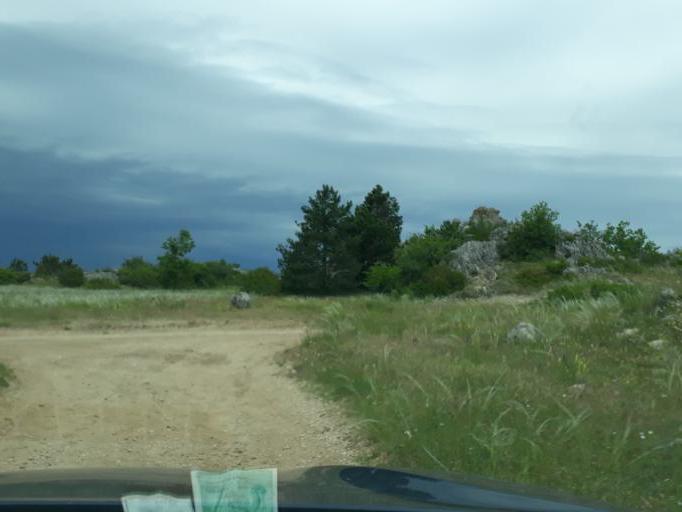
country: FR
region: Languedoc-Roussillon
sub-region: Departement de l'Herault
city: Lodeve
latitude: 43.8193
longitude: 3.2765
